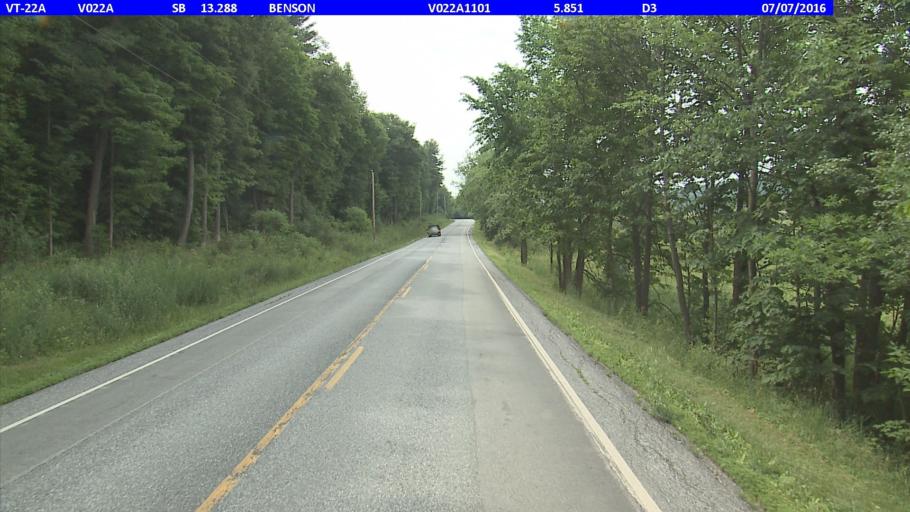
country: US
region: New York
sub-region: Essex County
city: Ticonderoga
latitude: 43.7517
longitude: -73.3087
